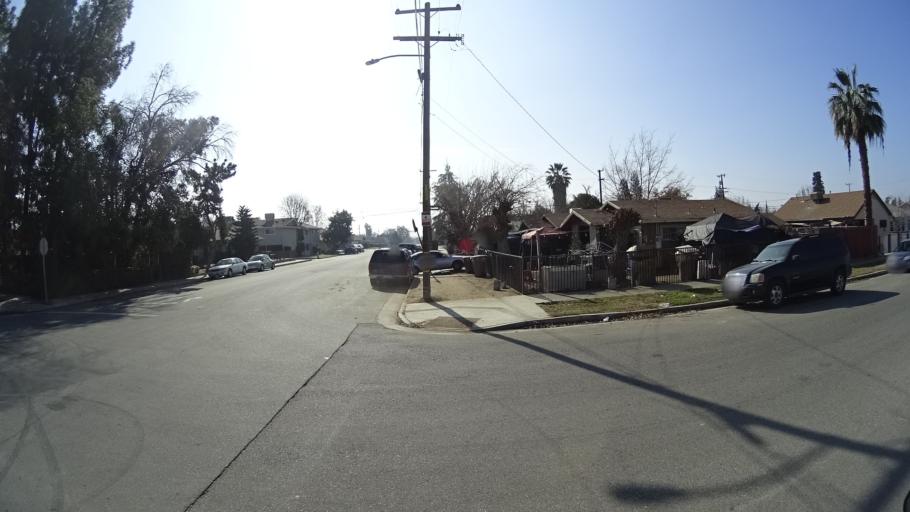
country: US
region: California
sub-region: Kern County
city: Bakersfield
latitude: 35.3898
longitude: -118.9900
